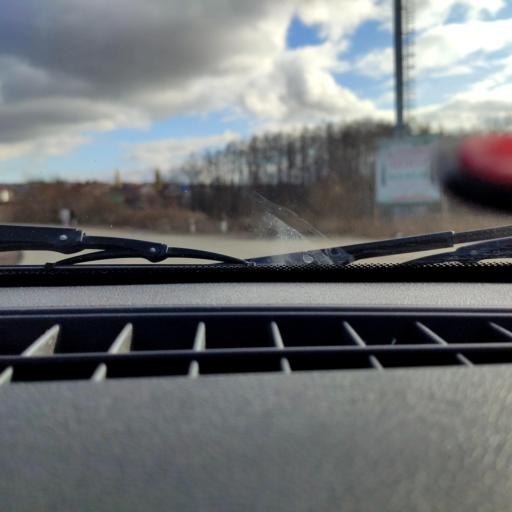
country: RU
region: Bashkortostan
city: Ufa
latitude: 54.5987
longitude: 55.9266
